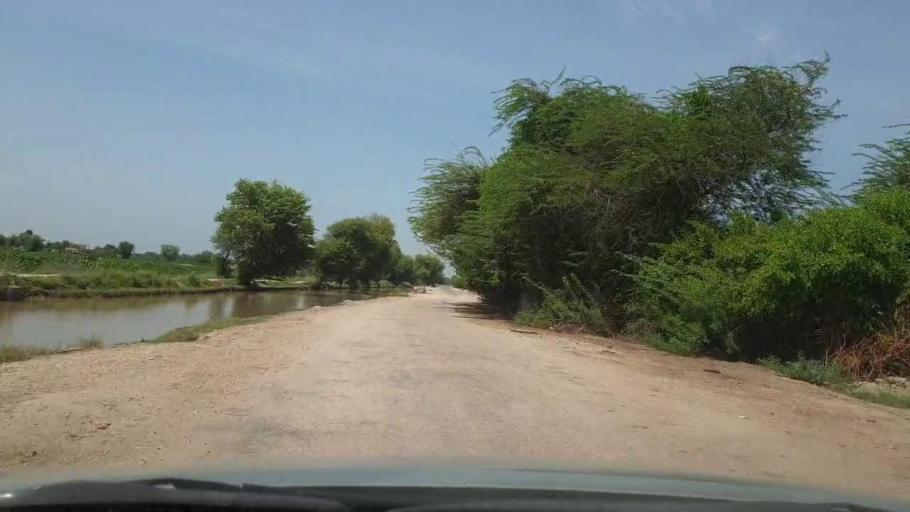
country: PK
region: Sindh
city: Pano Aqil
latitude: 27.6718
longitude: 69.1087
